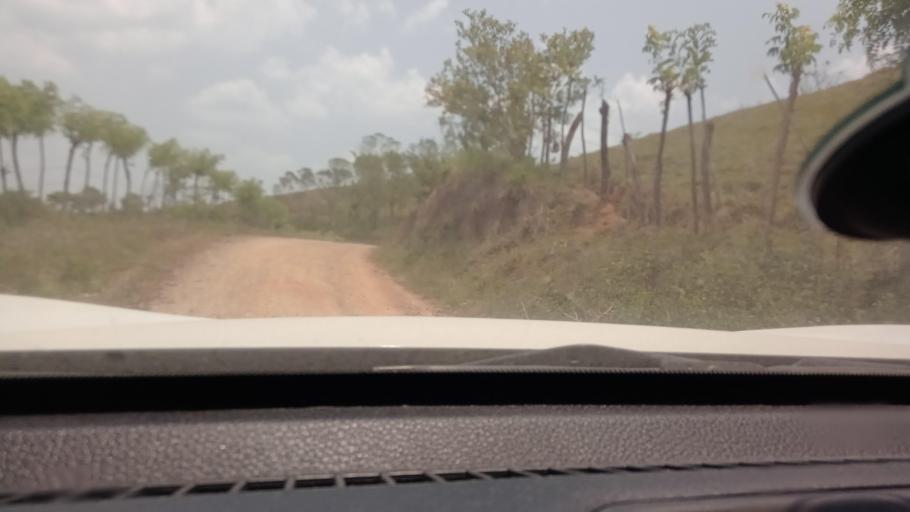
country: MX
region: Tabasco
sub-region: Huimanguillo
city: Francisco Rueda
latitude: 17.4933
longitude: -93.9214
